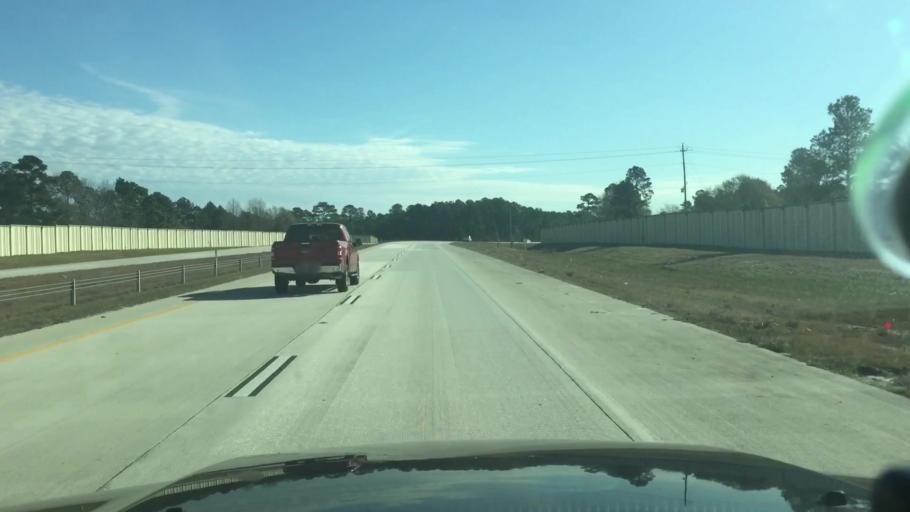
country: US
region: Texas
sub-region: Montgomery County
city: Porter Heights
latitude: 30.1376
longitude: -95.2622
